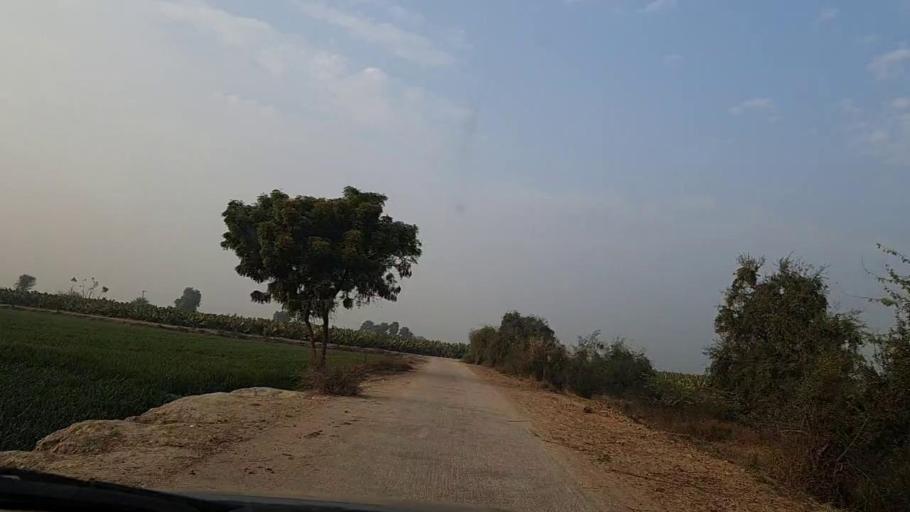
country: PK
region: Sindh
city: Nawabshah
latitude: 26.2959
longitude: 68.2767
